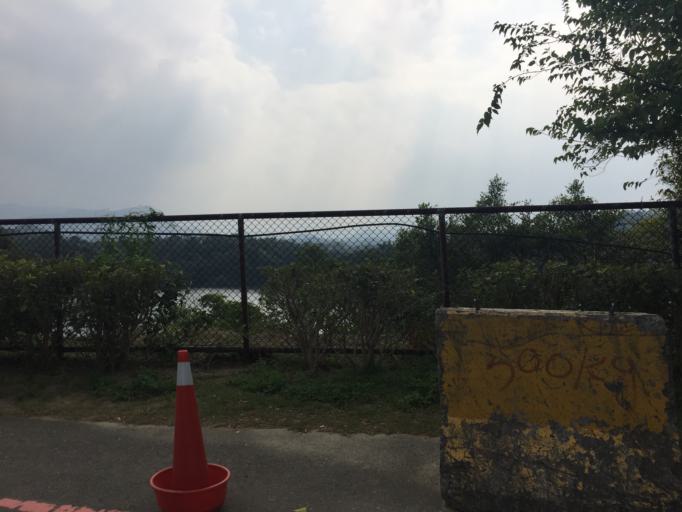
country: TW
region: Taiwan
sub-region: Hsinchu
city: Hsinchu
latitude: 24.6807
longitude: 120.9836
